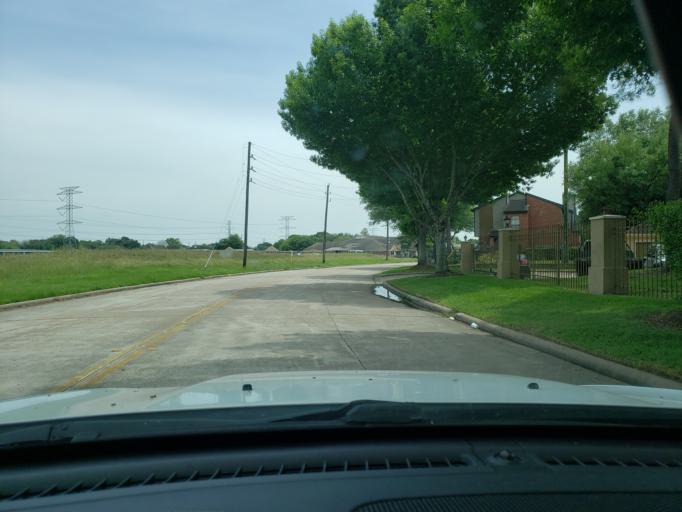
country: US
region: Texas
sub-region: Harris County
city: Jersey Village
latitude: 29.9121
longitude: -95.5803
